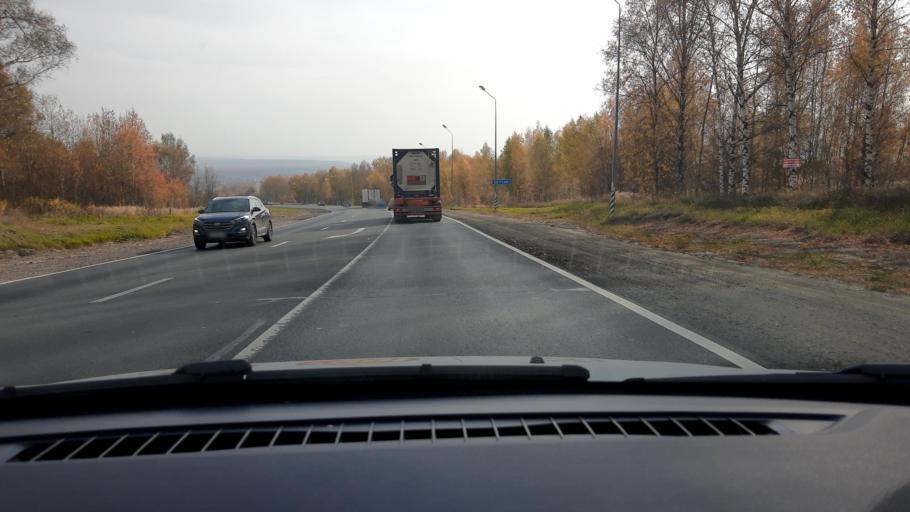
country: RU
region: Nizjnij Novgorod
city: Kstovo
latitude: 56.1072
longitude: 44.2878
